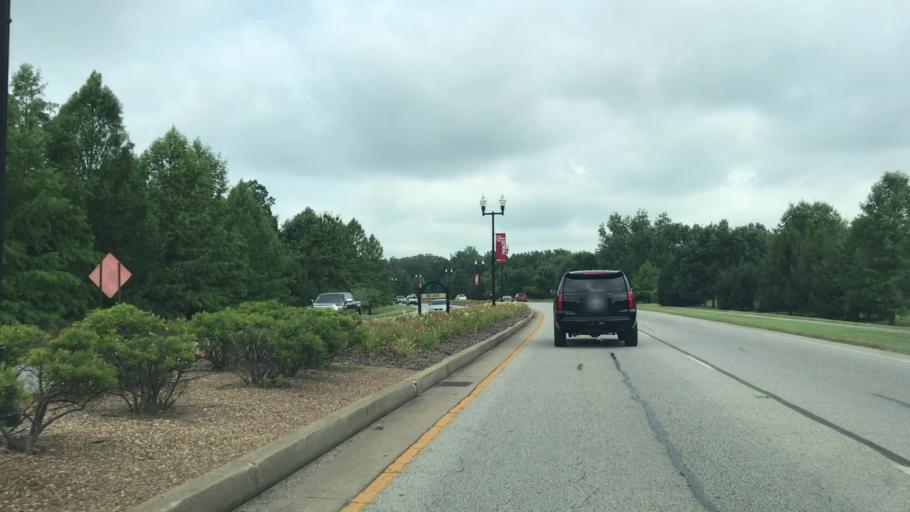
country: US
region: Kentucky
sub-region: Warren County
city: Bowling Green
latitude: 36.9830
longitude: -86.3974
